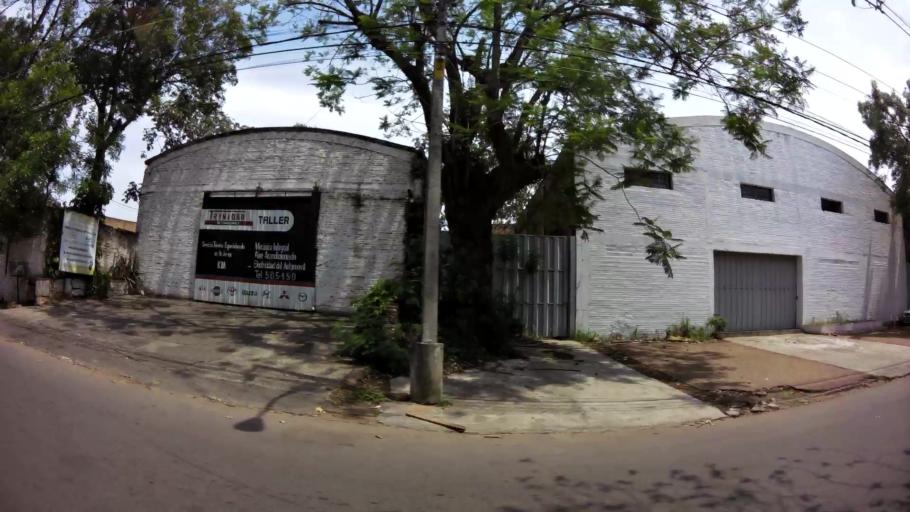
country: PY
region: Central
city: Fernando de la Mora
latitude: -25.3161
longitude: -57.5663
